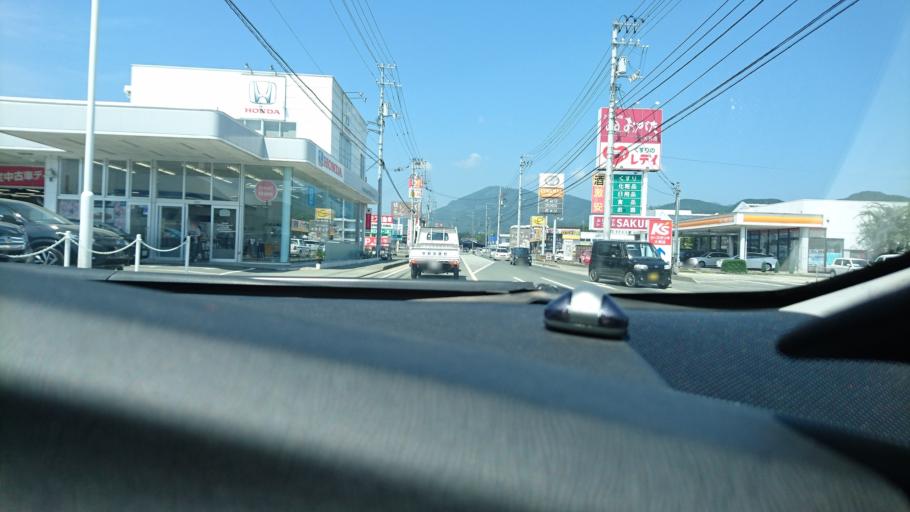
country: JP
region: Ehime
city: Ozu
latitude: 33.5274
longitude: 132.5643
